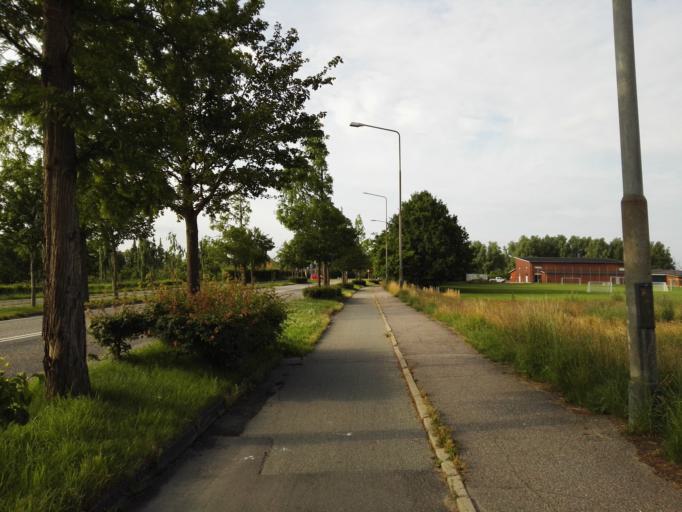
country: DK
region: Capital Region
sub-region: Ballerup Kommune
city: Ballerup
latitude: 55.7444
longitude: 12.3673
